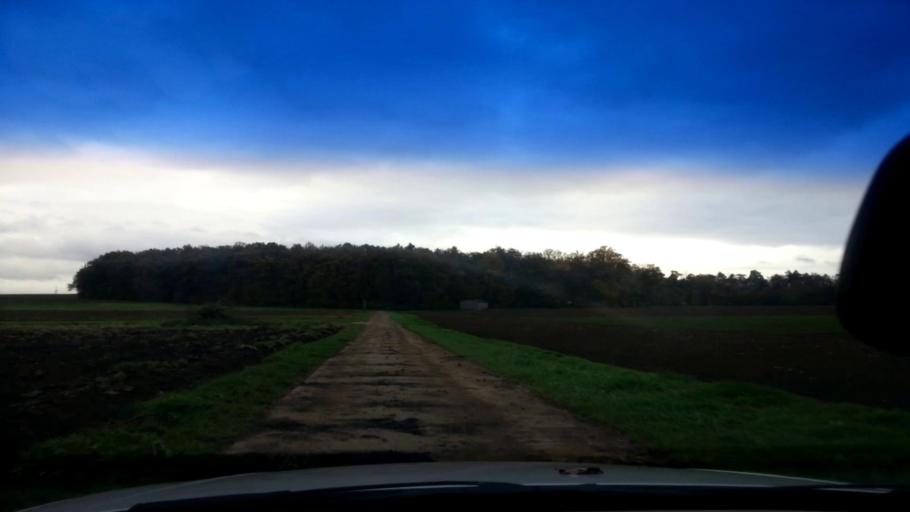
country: DE
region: Bavaria
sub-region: Upper Franconia
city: Gundelsheim
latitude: 49.9563
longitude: 10.9421
